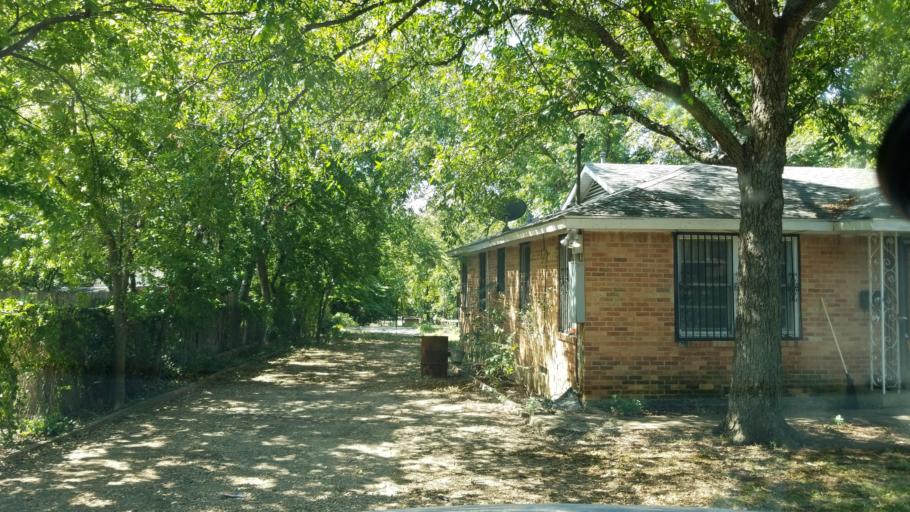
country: US
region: Texas
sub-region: Dallas County
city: Cockrell Hill
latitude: 32.7410
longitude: -96.8833
